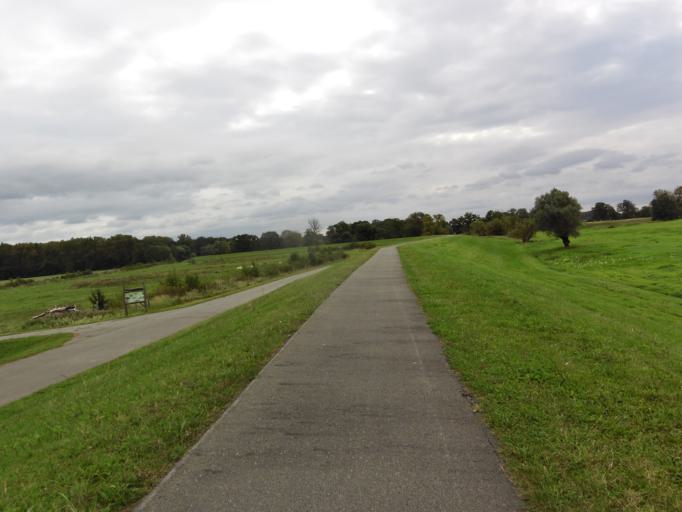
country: DE
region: Brandenburg
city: Ruhstadt
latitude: 52.9167
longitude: 11.8433
